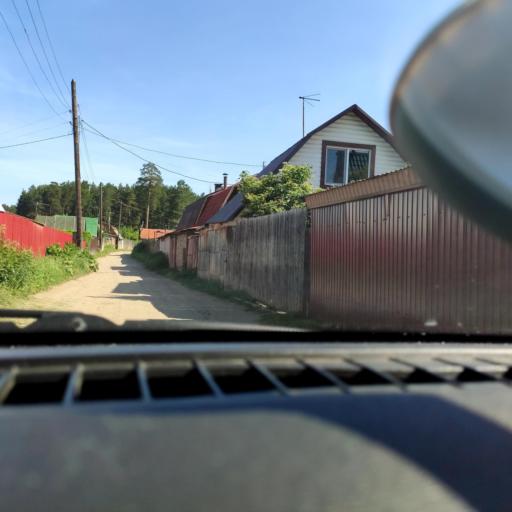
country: RU
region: Perm
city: Overyata
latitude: 58.0055
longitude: 55.8705
